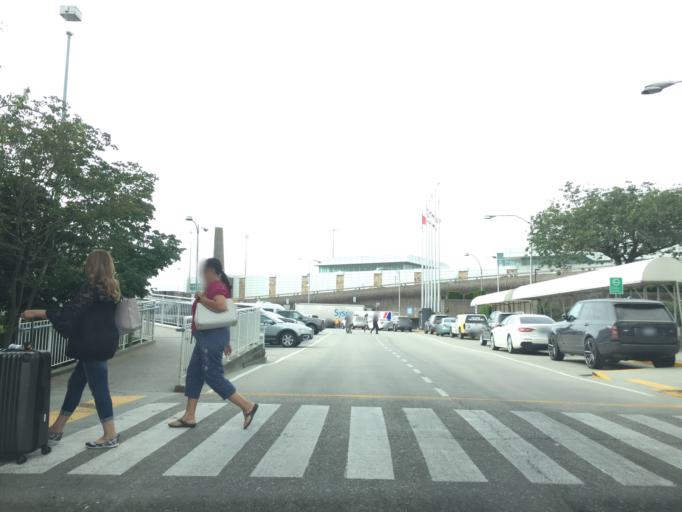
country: CA
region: British Columbia
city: Richmond
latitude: 49.1936
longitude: -123.1798
